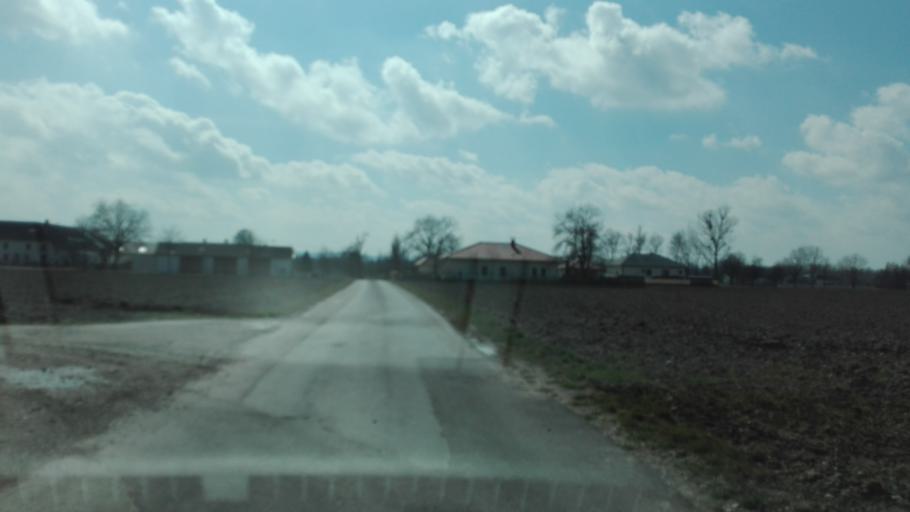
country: AT
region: Upper Austria
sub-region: Politischer Bezirk Urfahr-Umgebung
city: Feldkirchen an der Donau
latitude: 48.3432
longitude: 14.0458
